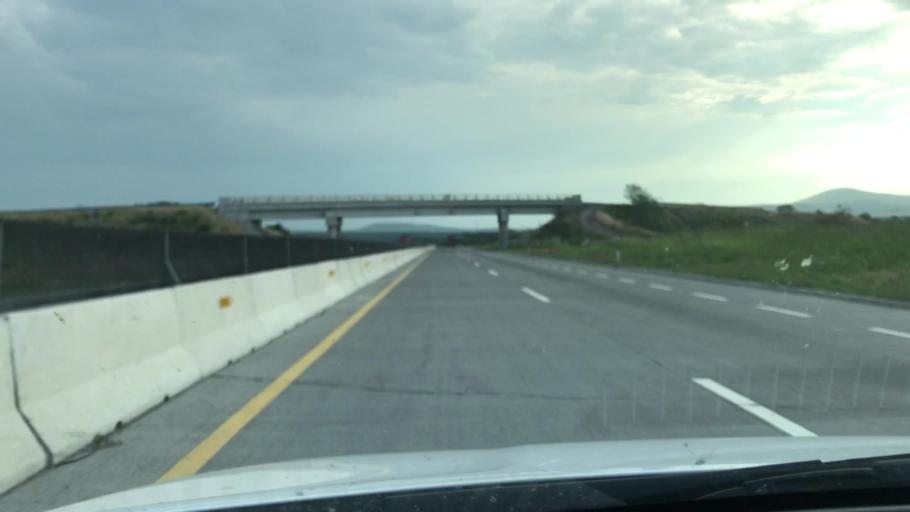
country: MX
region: Jalisco
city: Degollado
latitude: 20.3870
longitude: -102.1114
